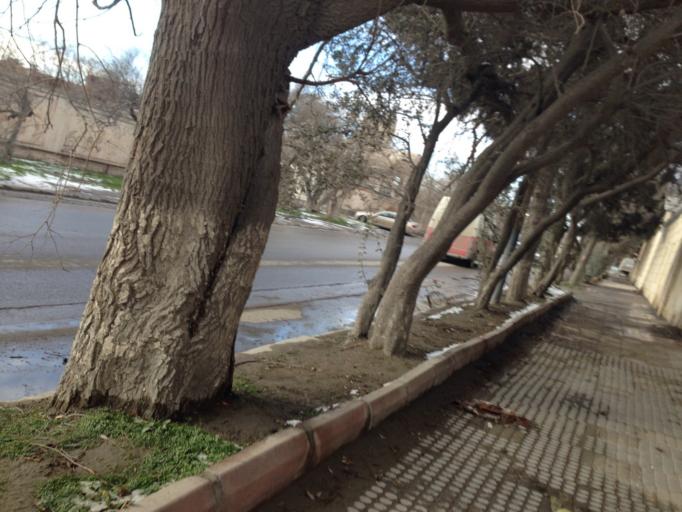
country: AZ
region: Baki
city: Baku
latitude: 40.3988
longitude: 49.8904
